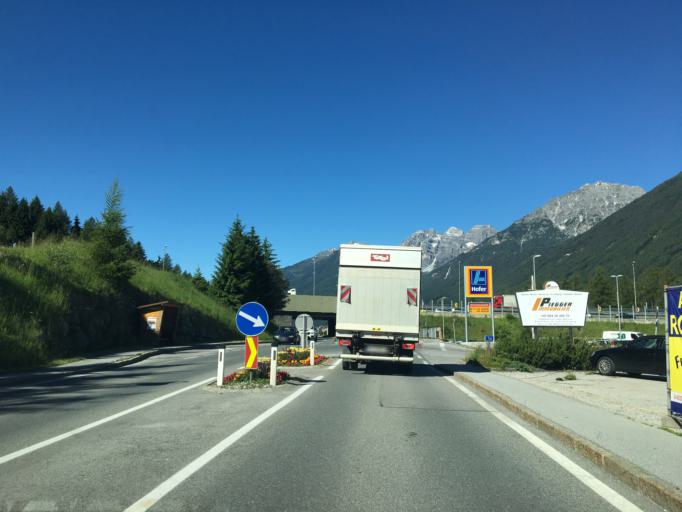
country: AT
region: Tyrol
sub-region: Politischer Bezirk Innsbruck Land
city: Schoenberg im Stubaital
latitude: 47.1829
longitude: 11.3990
